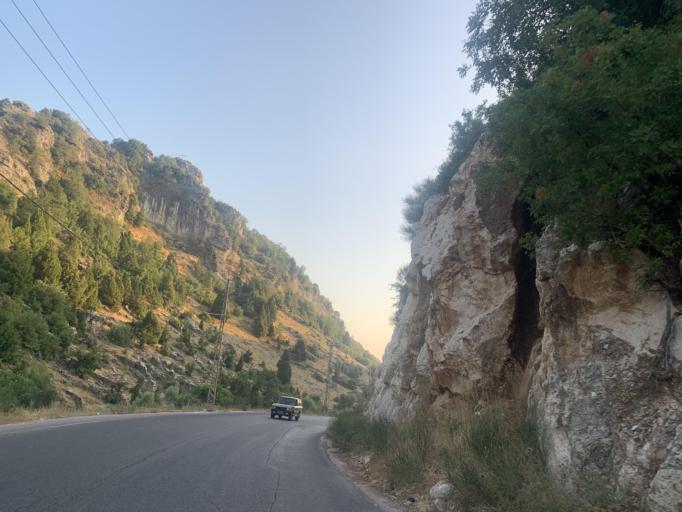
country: LB
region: Mont-Liban
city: Jbail
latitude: 34.1287
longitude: 35.8098
